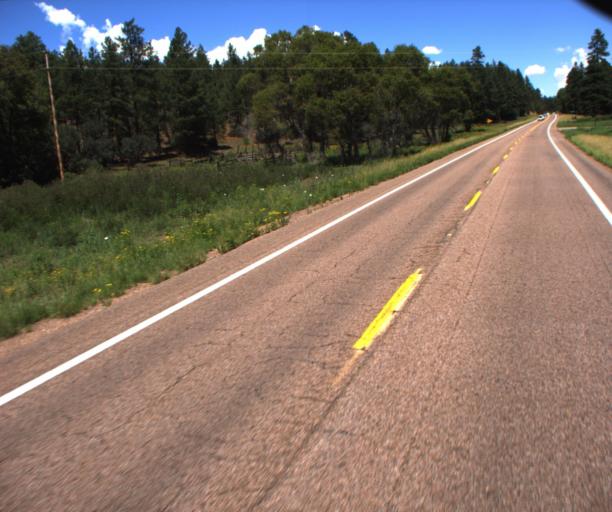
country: US
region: Arizona
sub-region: Navajo County
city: Lake of the Woods
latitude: 34.1432
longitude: -110.1053
